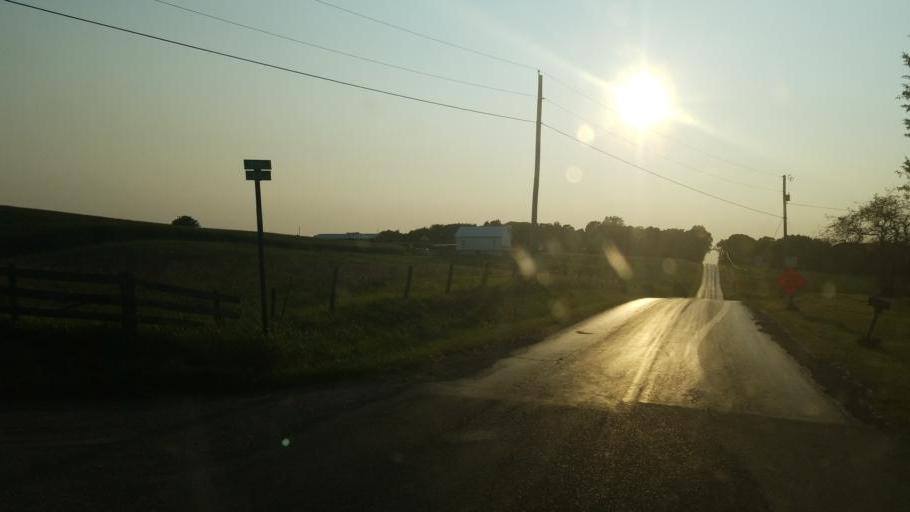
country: US
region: Ohio
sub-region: Wayne County
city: Shreve
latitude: 40.6680
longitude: -82.0049
